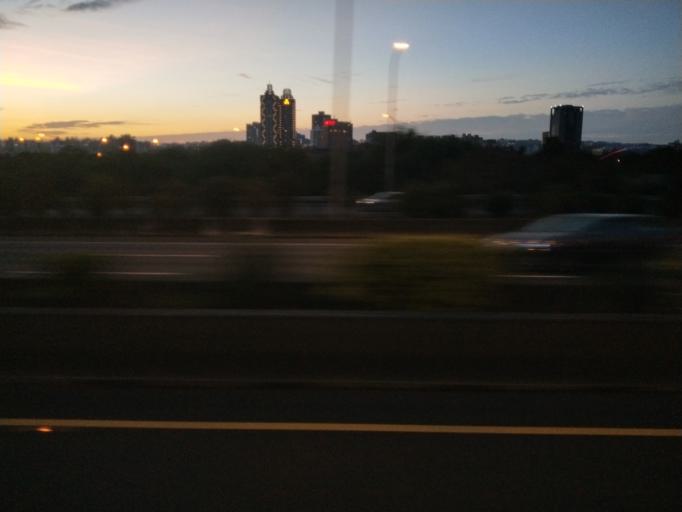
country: TW
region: Taiwan
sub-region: Taichung City
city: Taichung
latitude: 24.1763
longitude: 120.6319
